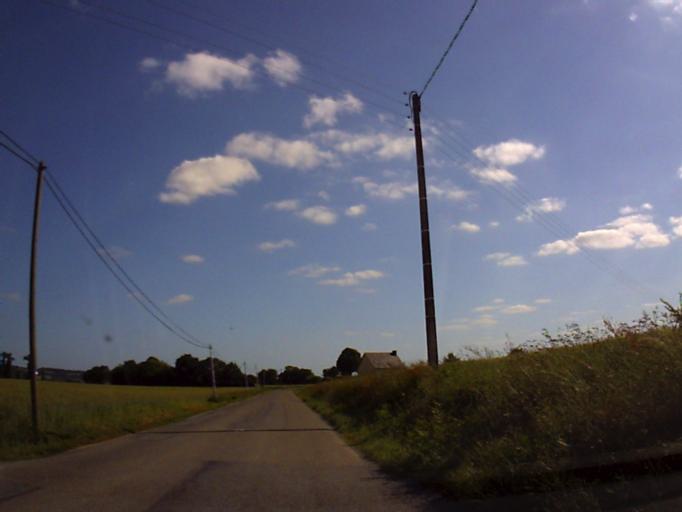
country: FR
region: Brittany
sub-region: Departement d'Ille-et-Vilaine
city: Iffendic
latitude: 48.1420
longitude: -2.0188
